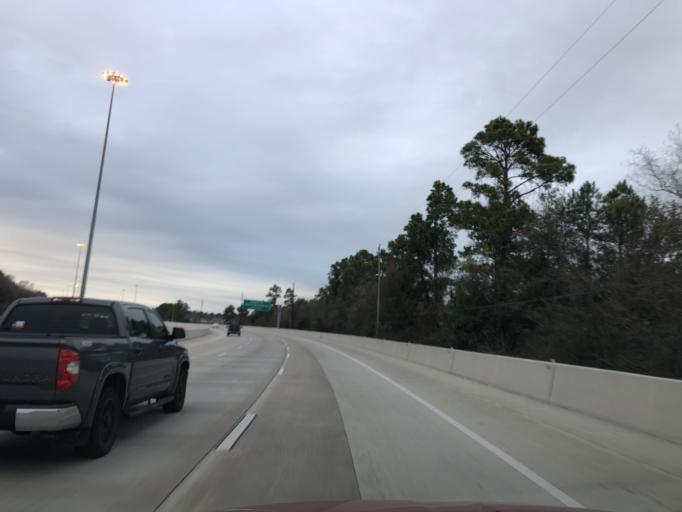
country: US
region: Texas
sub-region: Harris County
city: Spring
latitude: 30.0520
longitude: -95.4039
